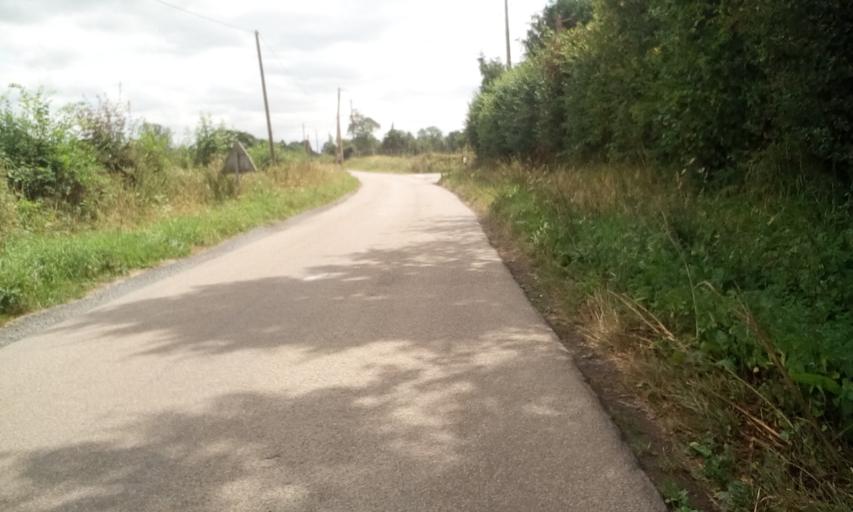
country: FR
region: Lower Normandy
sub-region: Departement du Calvados
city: Bavent
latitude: 49.2053
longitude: -0.1775
